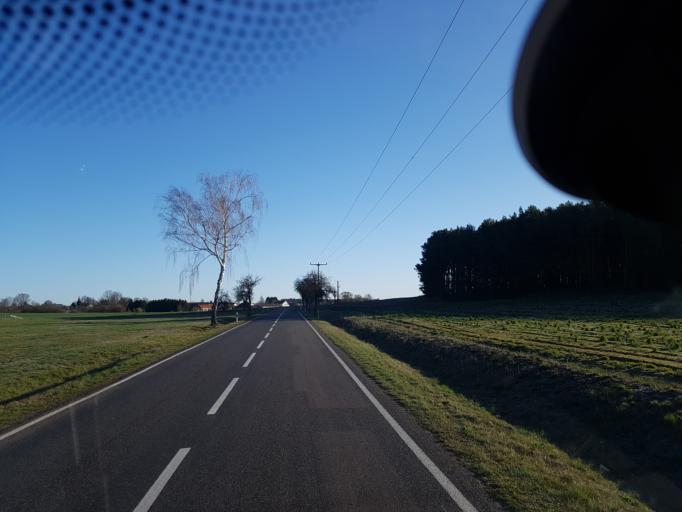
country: DE
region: Brandenburg
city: Jamlitz
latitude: 52.0567
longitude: 14.4309
